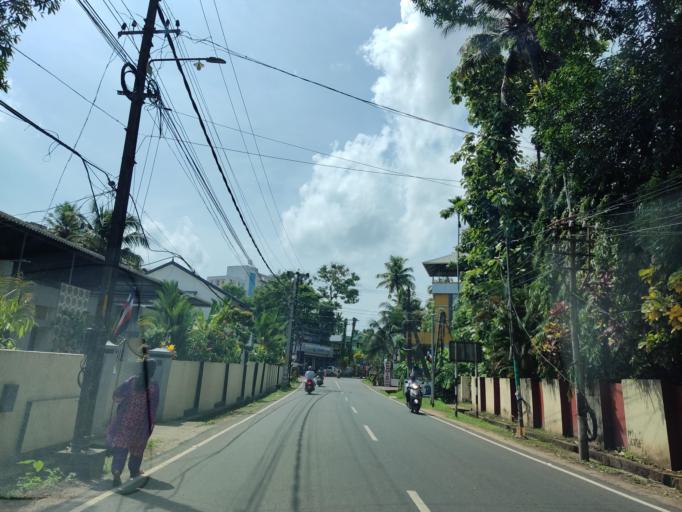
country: IN
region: Kerala
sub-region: Alappuzha
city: Mavelikara
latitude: 9.2550
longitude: 76.5451
